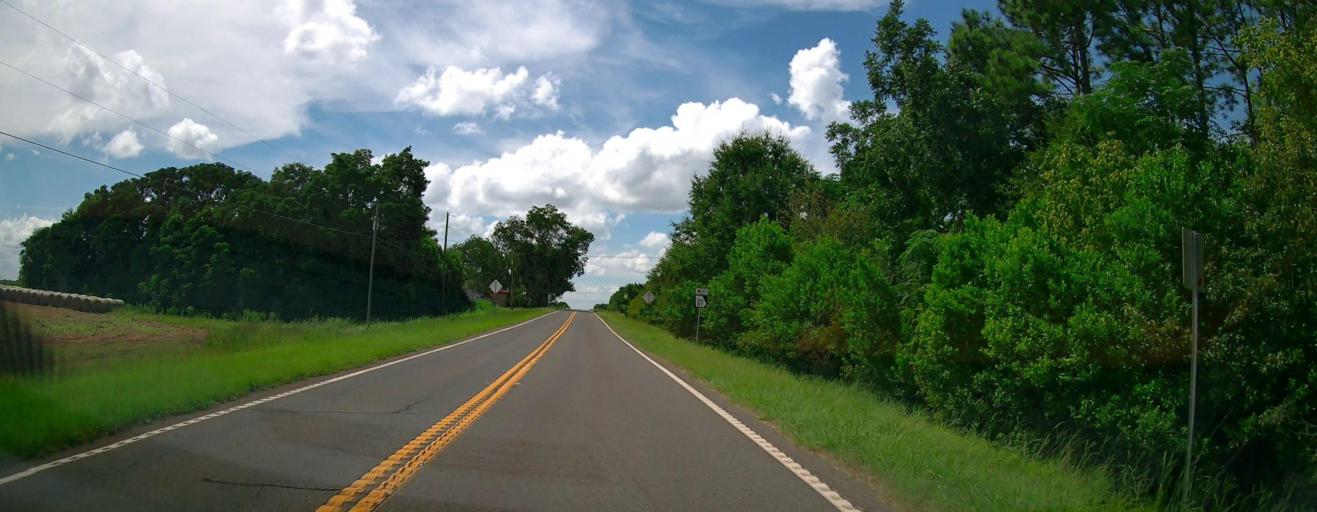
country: US
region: Georgia
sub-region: Macon County
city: Marshallville
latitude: 32.4325
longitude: -84.0044
